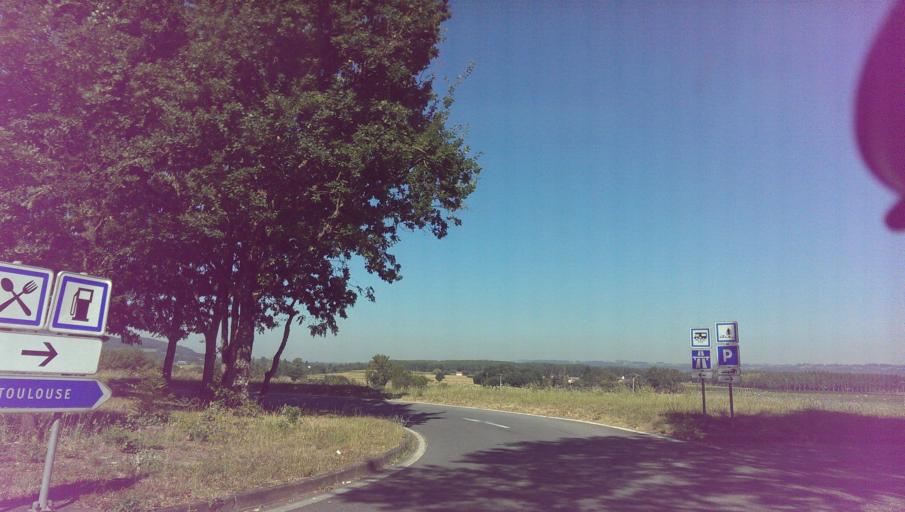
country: FR
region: Aquitaine
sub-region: Departement du Lot-et-Garonne
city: Sainte-Colombe-en-Bruilhois
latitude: 44.2000
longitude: 0.5071
